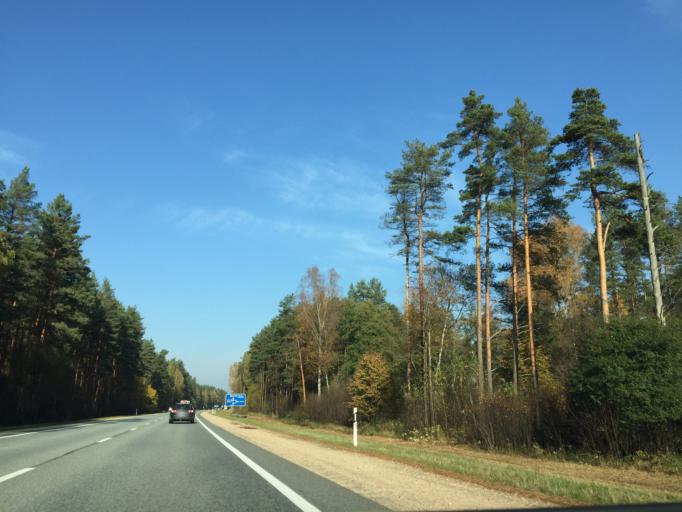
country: LV
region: Babite
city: Pinki
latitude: 56.9119
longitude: 23.9155
